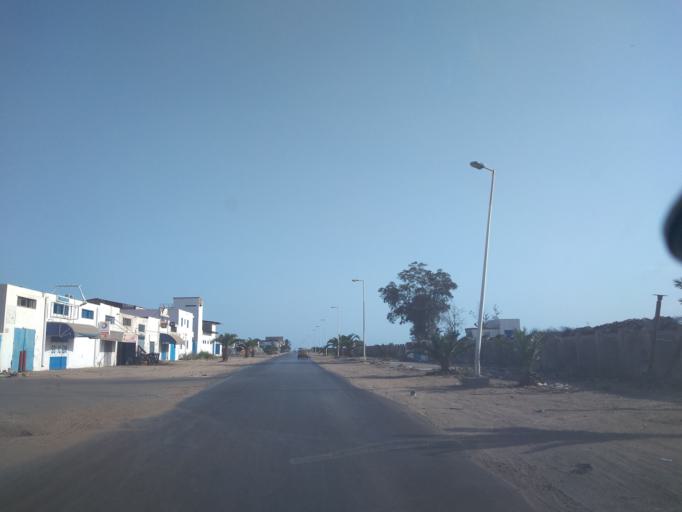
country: TN
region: Safaqis
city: Sfax
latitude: 34.7190
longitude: 10.7609
